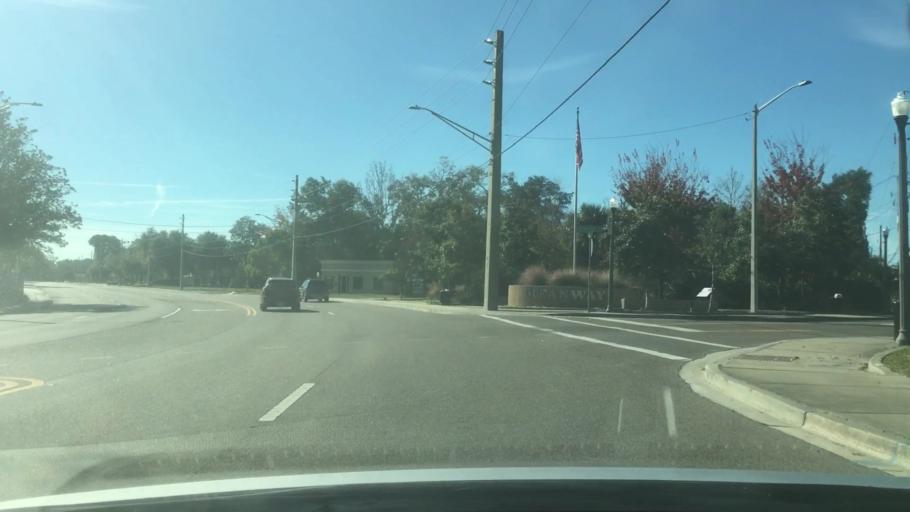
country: US
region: Florida
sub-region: Duval County
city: Jacksonville
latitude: 30.4664
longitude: -81.6274
